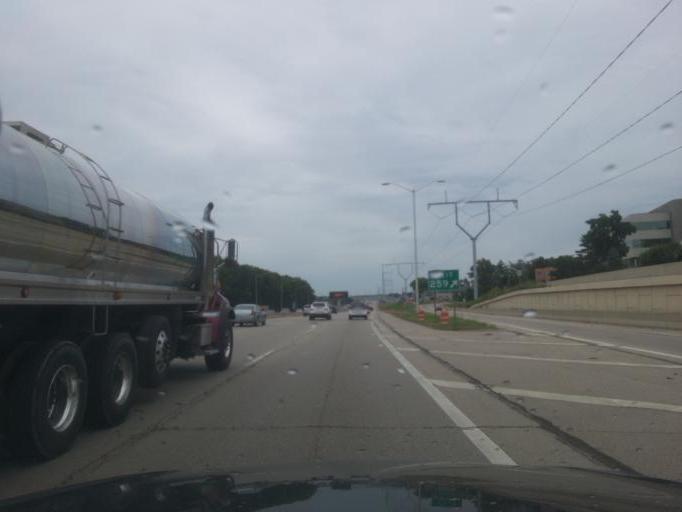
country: US
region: Wisconsin
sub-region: Dane County
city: Shorewood Hills
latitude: 43.0354
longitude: -89.4311
